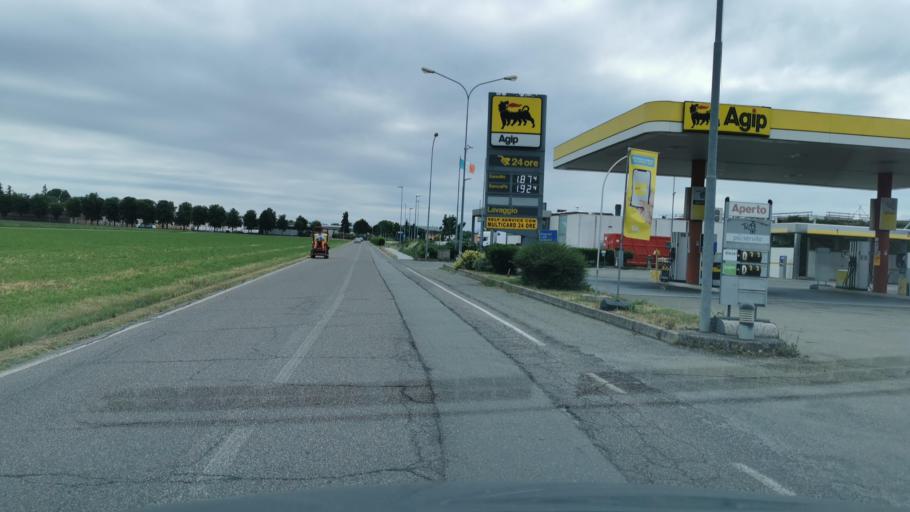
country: IT
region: Emilia-Romagna
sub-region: Provincia di Parma
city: Soragna
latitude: 44.9273
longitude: 10.1187
